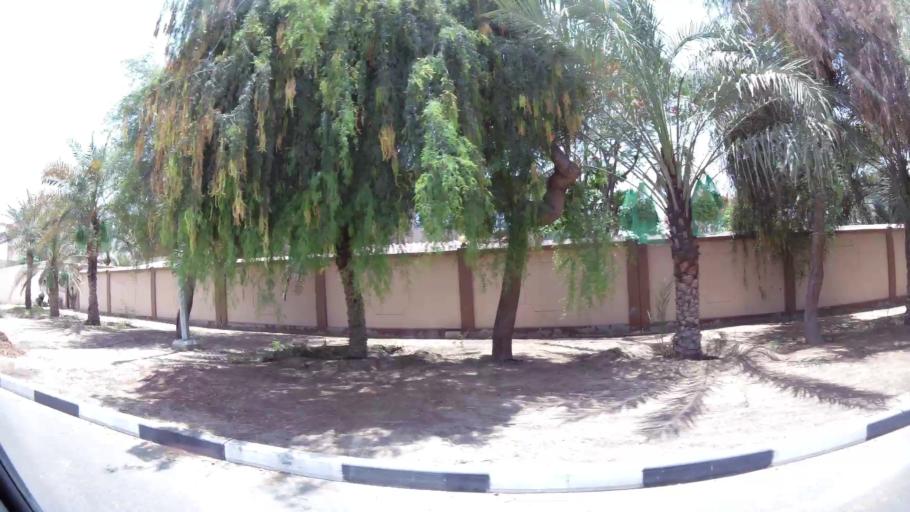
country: AE
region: Ash Shariqah
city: Sharjah
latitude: 25.2441
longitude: 55.4641
